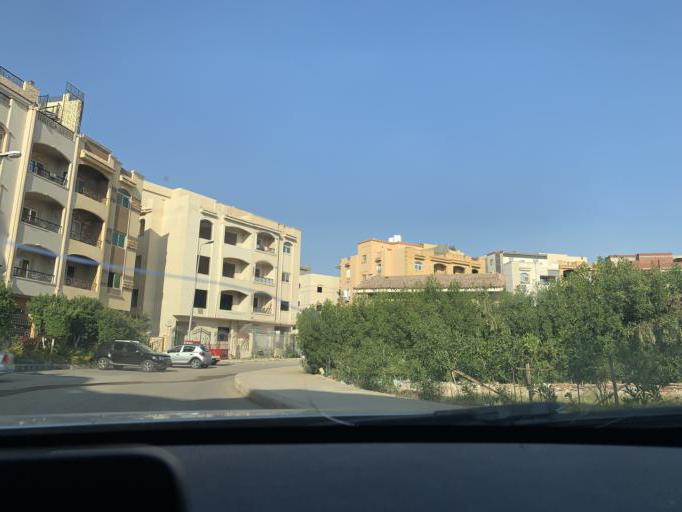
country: EG
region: Muhafazat al Qalyubiyah
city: Al Khankah
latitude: 30.0032
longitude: 31.4813
